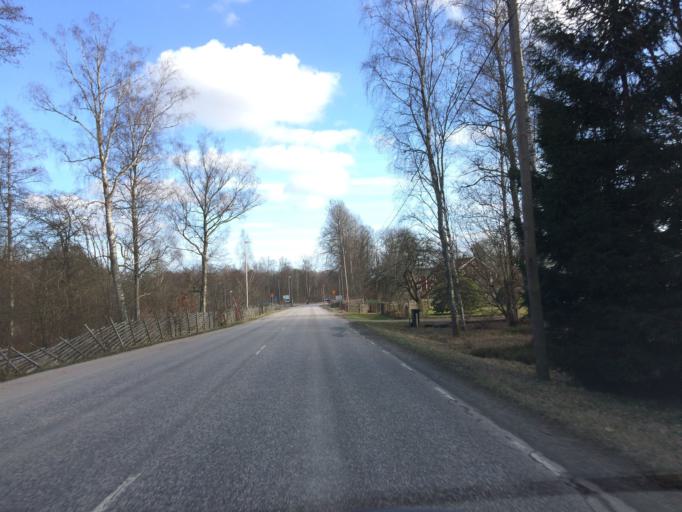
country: SE
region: Kronoberg
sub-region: Almhults Kommun
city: AElmhult
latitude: 56.5673
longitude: 14.1244
